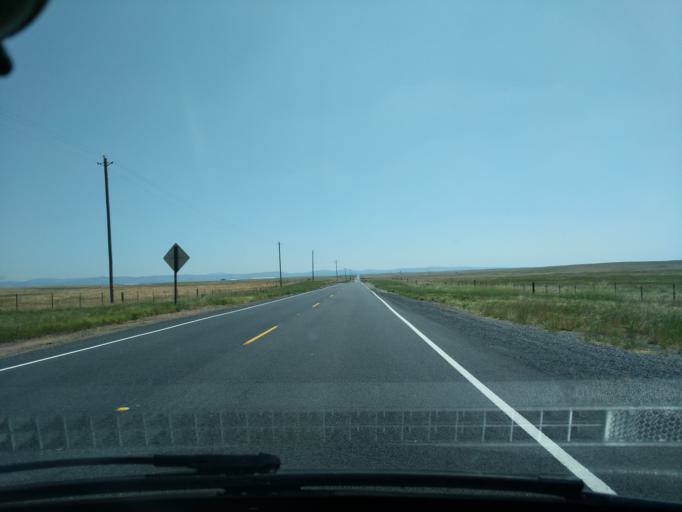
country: US
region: California
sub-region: San Joaquin County
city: Escalon
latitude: 37.9448
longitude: -120.9383
